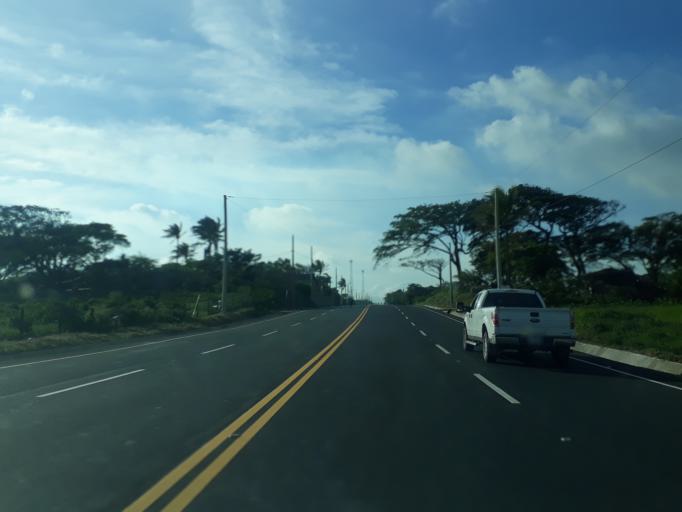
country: NI
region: Carazo
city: Diriamba
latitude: 11.9201
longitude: -86.2785
